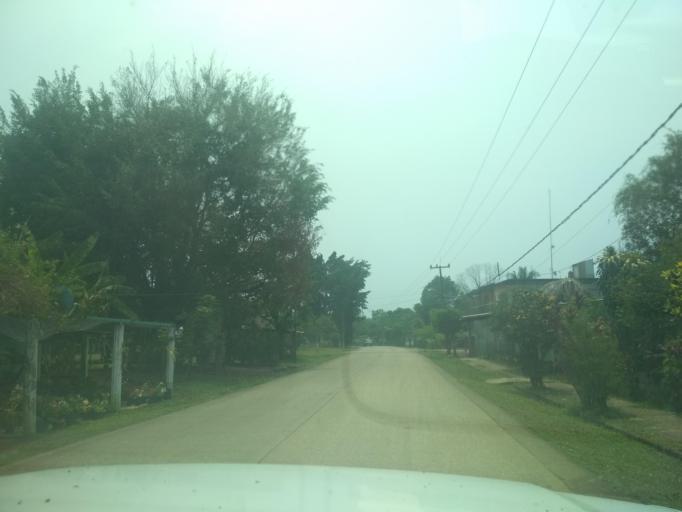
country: MX
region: Veracruz
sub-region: Tezonapa
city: Laguna Chica (Pueblo Nuevo)
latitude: 18.5158
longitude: -96.7776
